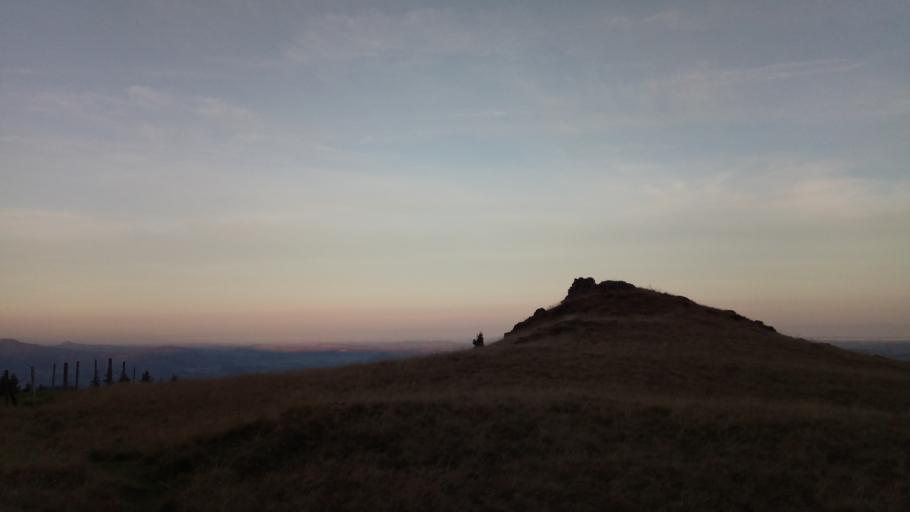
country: CH
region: Bern
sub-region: Interlaken-Oberhasli District
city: Beatenberg
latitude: 46.7492
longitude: 7.7924
